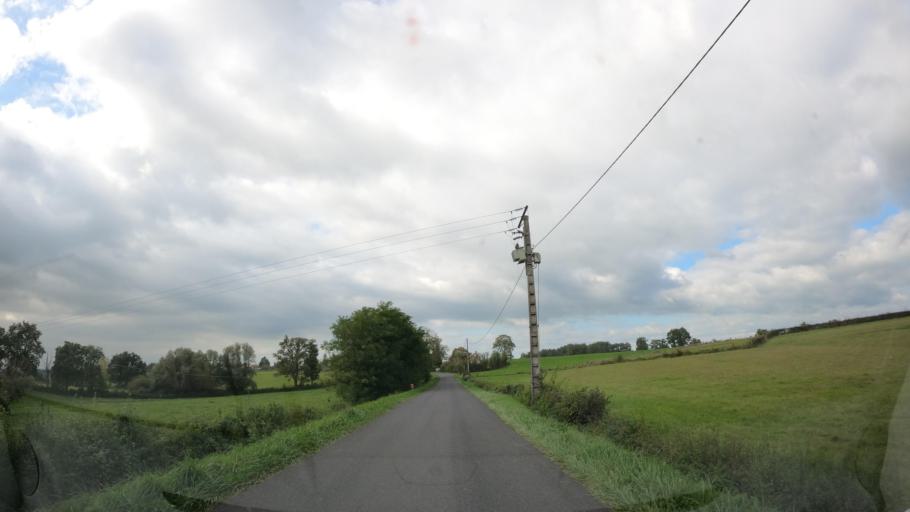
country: FR
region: Auvergne
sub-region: Departement de l'Allier
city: Lapalisse
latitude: 46.3473
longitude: 3.6294
